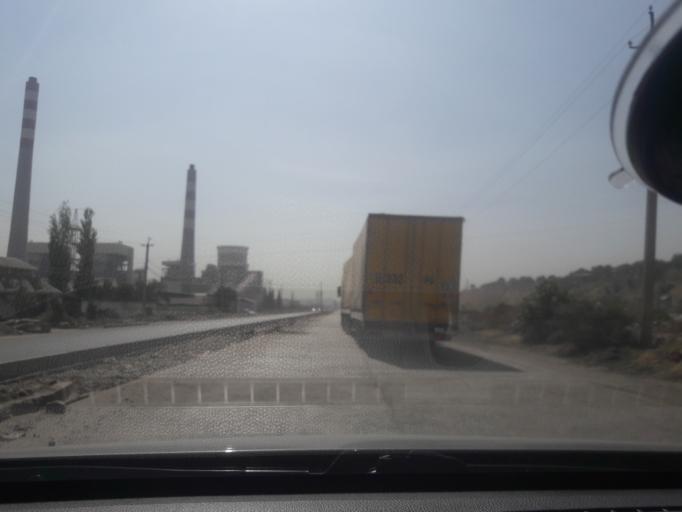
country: TJ
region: Dushanbe
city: Dushanbe
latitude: 38.6144
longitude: 68.7692
